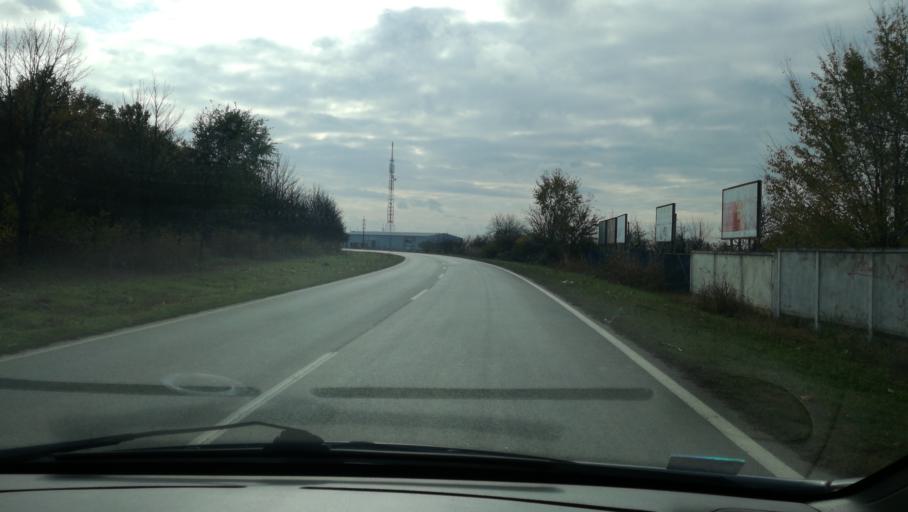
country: RS
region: Autonomna Pokrajina Vojvodina
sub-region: Severnobanatski Okrug
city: Kikinda
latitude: 45.8123
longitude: 20.4327
